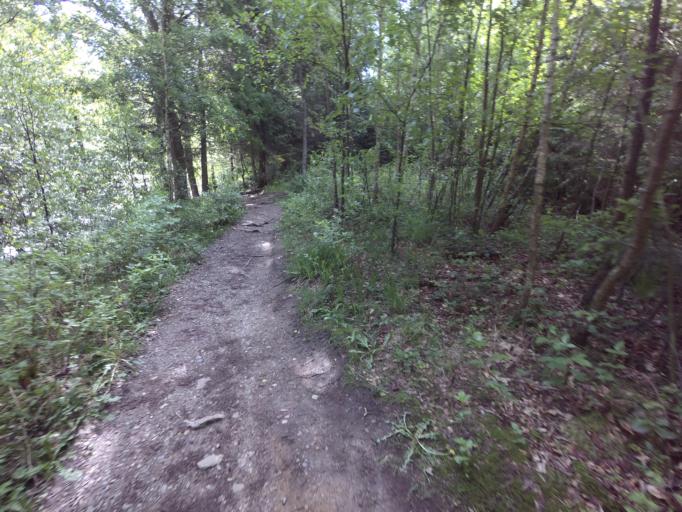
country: BE
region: Wallonia
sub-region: Province de Liege
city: Jalhay
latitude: 50.5027
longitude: 5.9658
